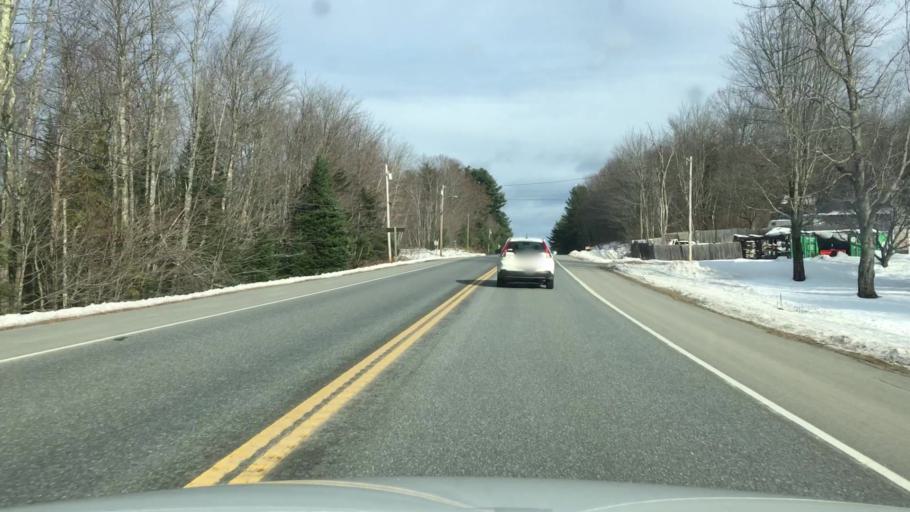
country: US
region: Maine
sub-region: Kennebec County
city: Monmouth
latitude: 44.2562
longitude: -70.0582
